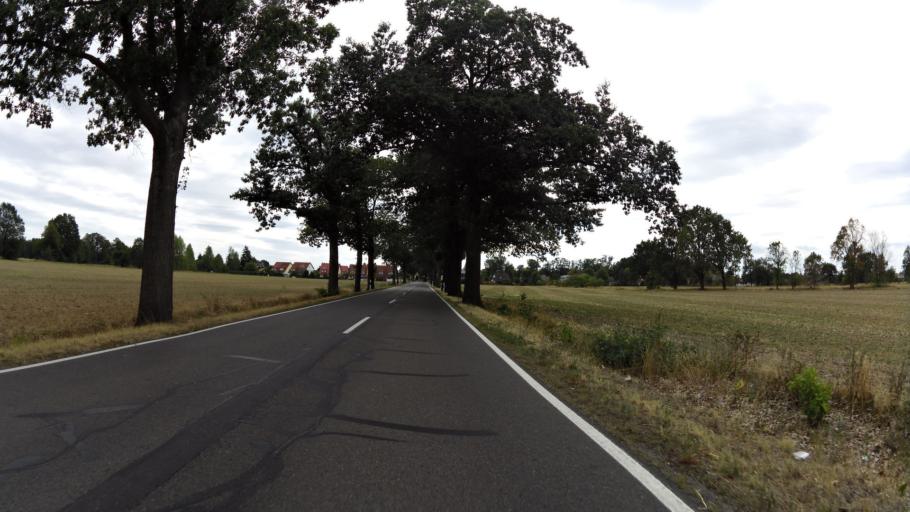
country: DE
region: Brandenburg
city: Cottbus
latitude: 51.7266
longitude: 14.4168
